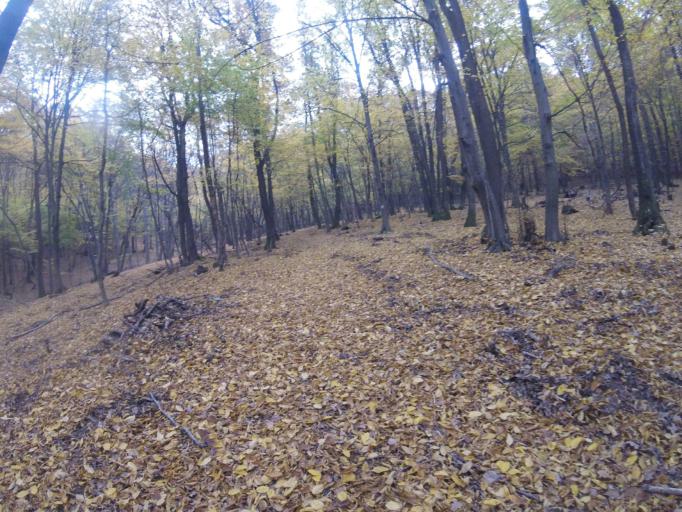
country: HU
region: Borsod-Abauj-Zemplen
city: Gonc
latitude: 48.4619
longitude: 21.3086
